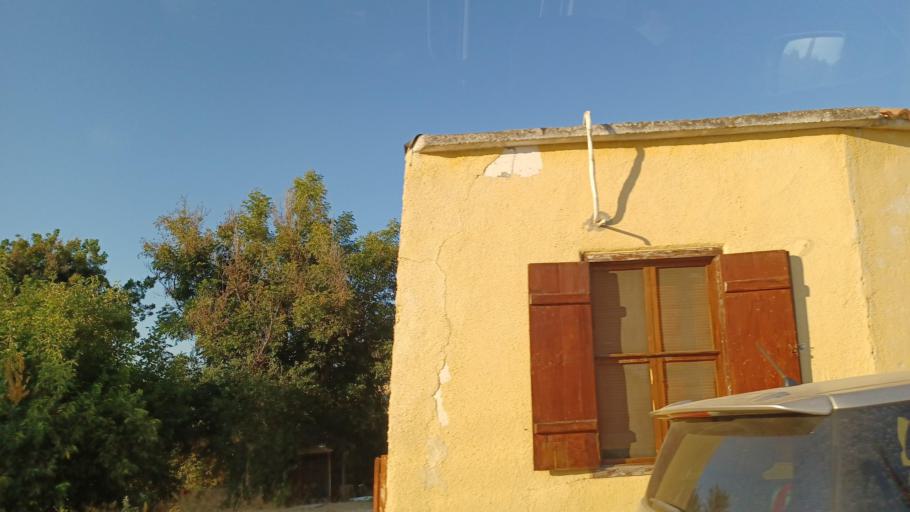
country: CY
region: Pafos
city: Polis
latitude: 35.0032
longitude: 32.4409
